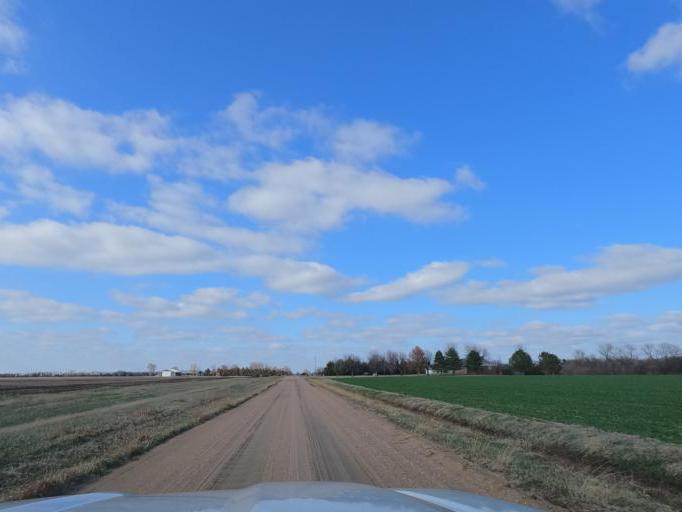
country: US
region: Kansas
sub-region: McPherson County
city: Inman
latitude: 38.2346
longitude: -97.8669
